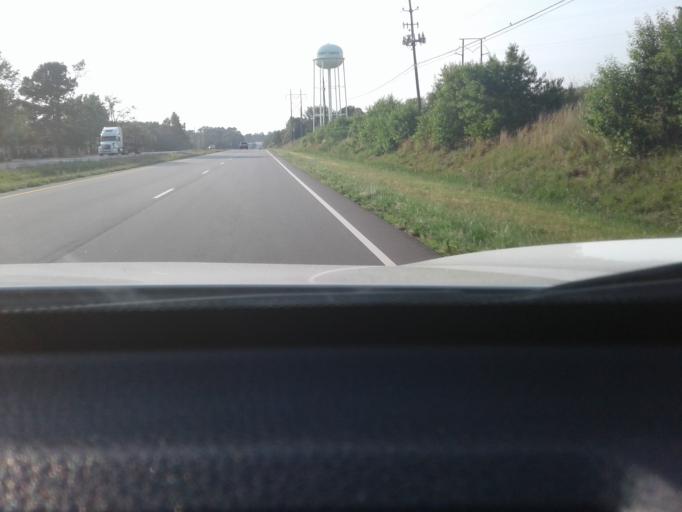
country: US
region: North Carolina
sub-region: Harnett County
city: Erwin
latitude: 35.3690
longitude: -78.7061
